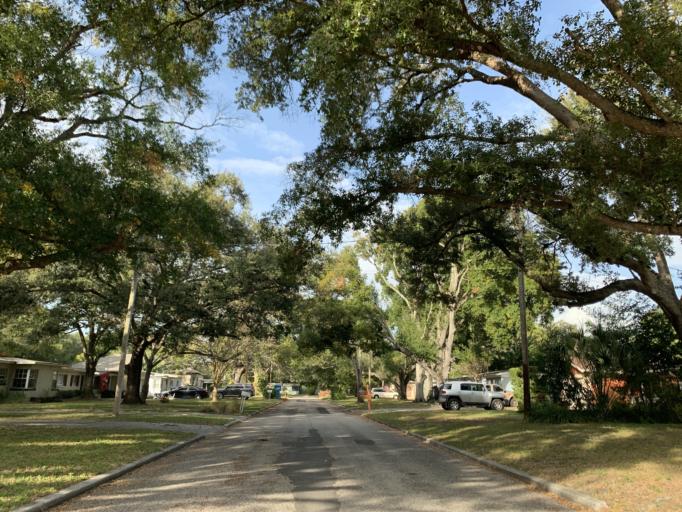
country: US
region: Florida
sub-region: Hillsborough County
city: Tampa
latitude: 27.9029
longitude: -82.5148
